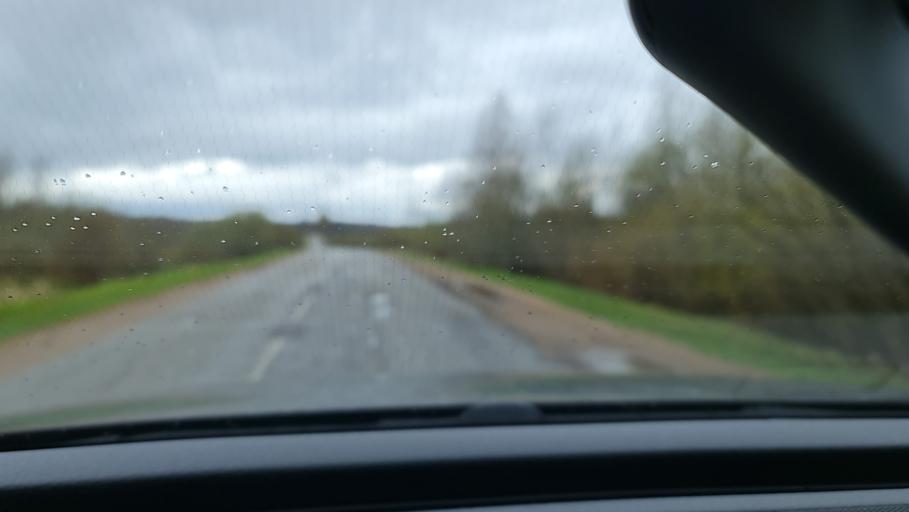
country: RU
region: Novgorod
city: Marevo
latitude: 57.2448
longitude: 32.0553
